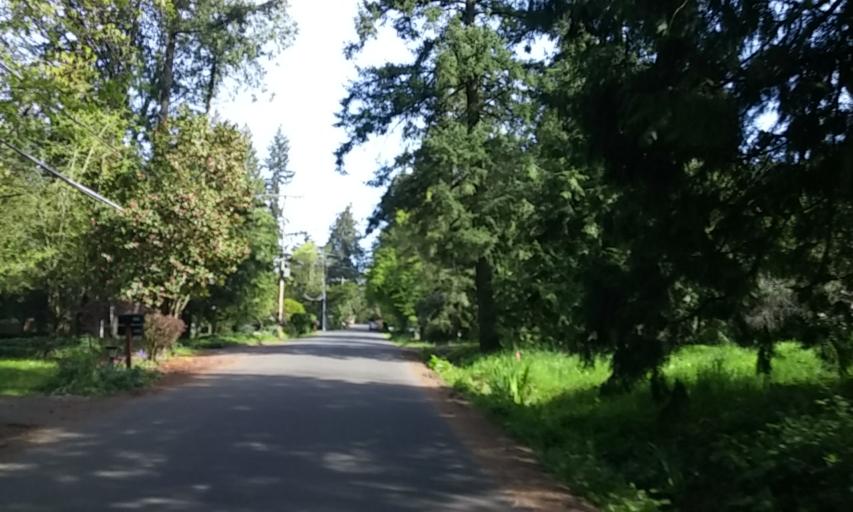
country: US
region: Oregon
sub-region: Washington County
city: West Slope
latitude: 45.5009
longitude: -122.7666
